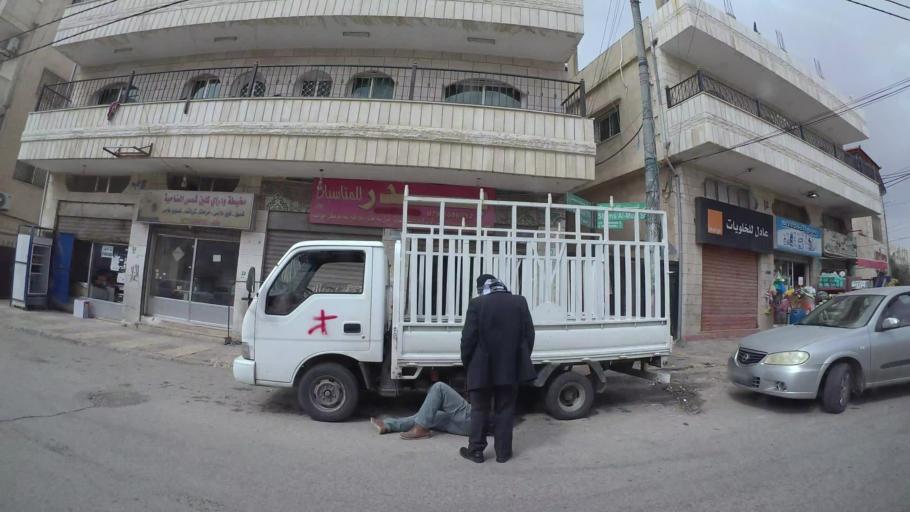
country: JO
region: Amman
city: Amman
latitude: 31.9842
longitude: 35.9217
